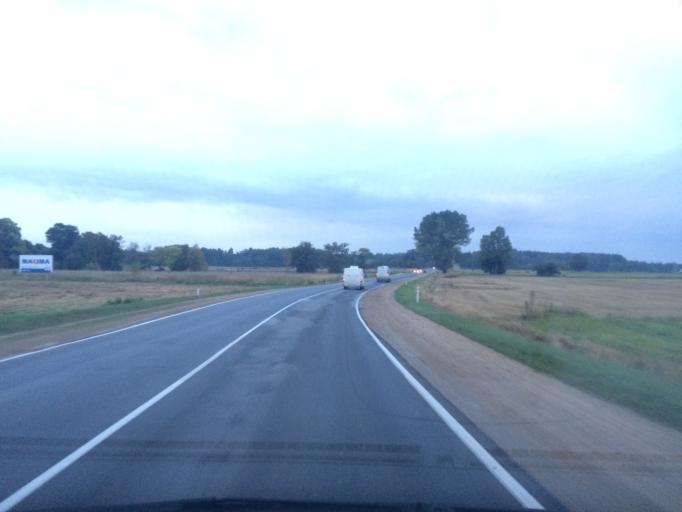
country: LV
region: Jekabpils Rajons
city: Jekabpils
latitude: 56.5241
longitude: 25.8378
